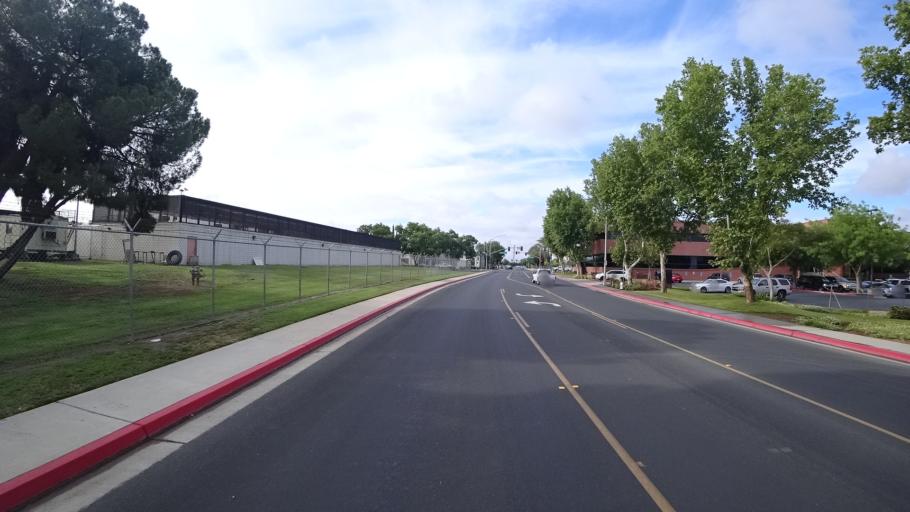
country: US
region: California
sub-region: Kings County
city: Hanford
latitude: 36.3292
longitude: -119.6685
